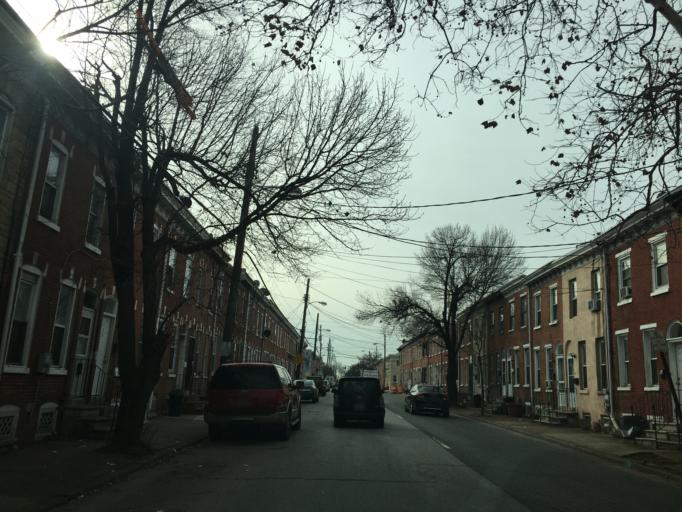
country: US
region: Delaware
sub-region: New Castle County
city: Wilmington
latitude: 39.7425
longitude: -75.5404
